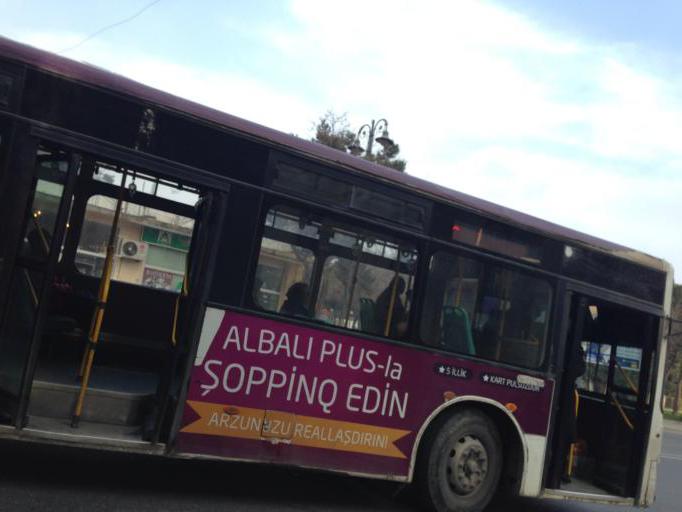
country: AZ
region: Baki
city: Baku
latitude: 40.4023
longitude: 49.8604
